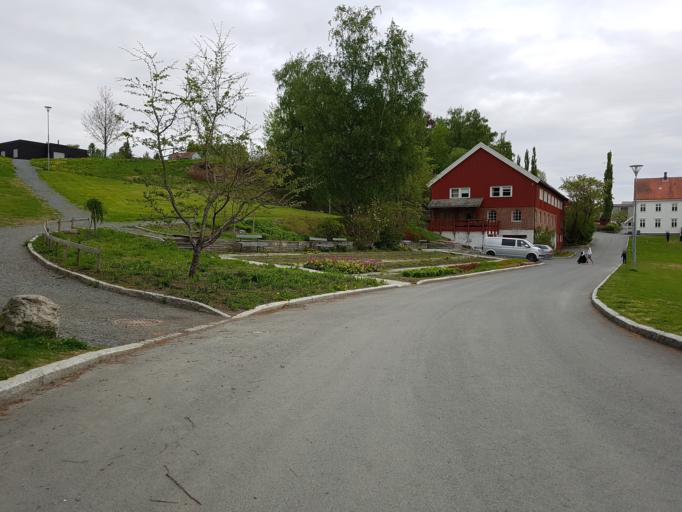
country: NO
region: Nord-Trondelag
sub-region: Levanger
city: Levanger
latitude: 63.7453
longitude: 11.2772
